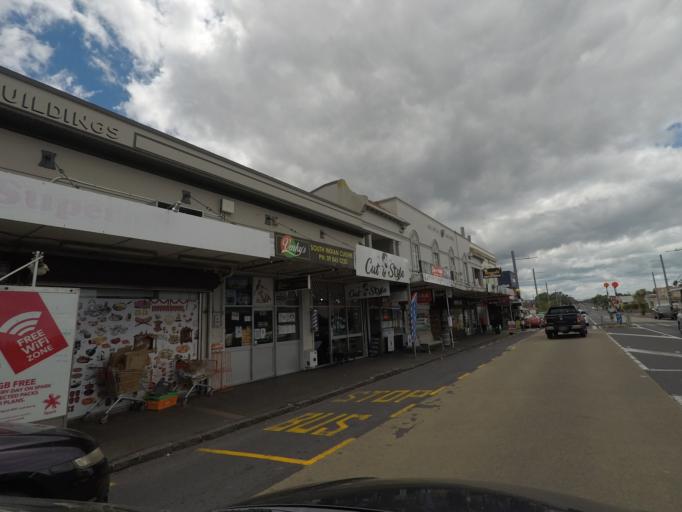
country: NZ
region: Auckland
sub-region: Auckland
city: Auckland
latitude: -36.8919
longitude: 174.7362
